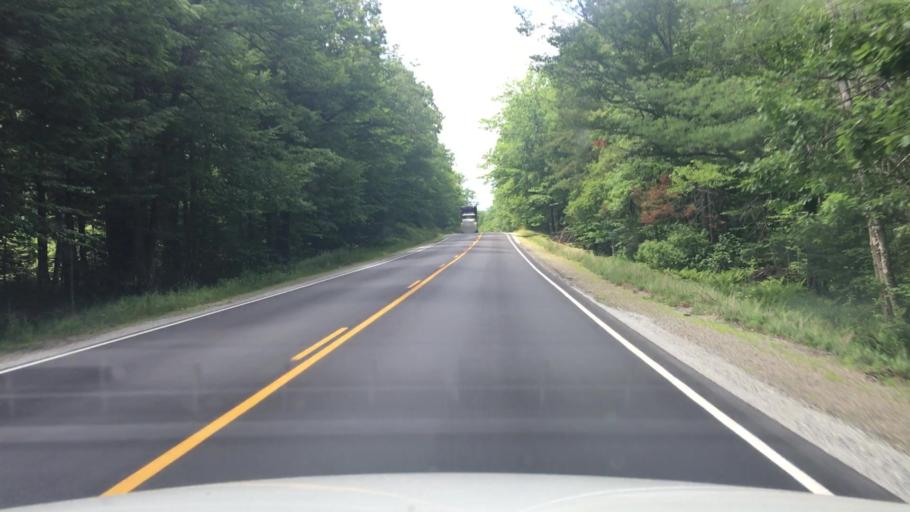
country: US
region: Maine
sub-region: Oxford County
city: West Paris
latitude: 44.3961
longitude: -70.6673
